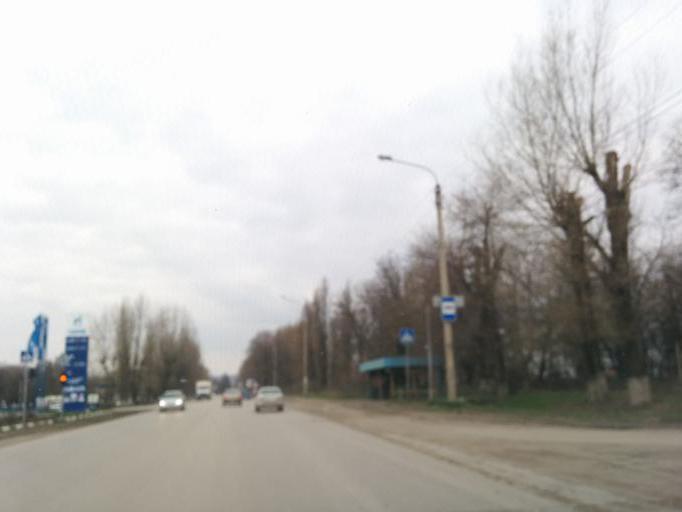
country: RU
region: Rostov
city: Novocherkassk
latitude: 47.4688
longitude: 40.1004
